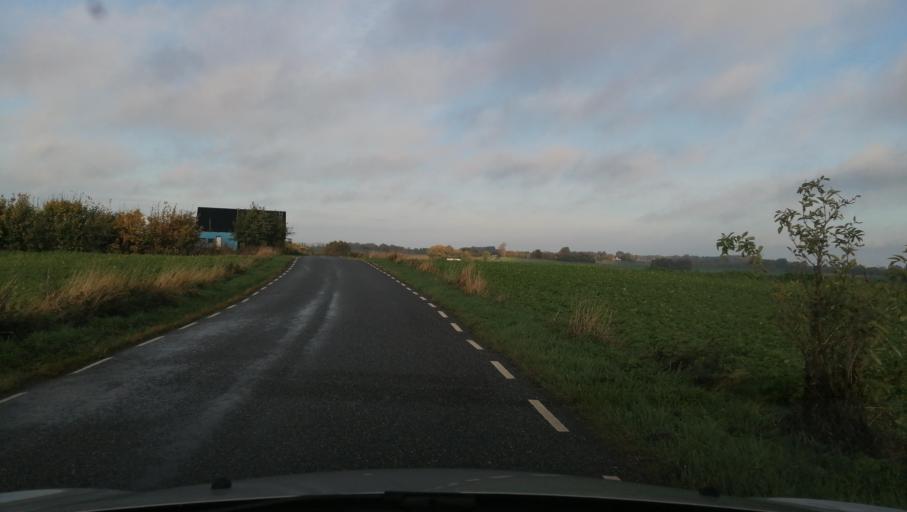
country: DK
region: Zealand
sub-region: Odsherred Kommune
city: Horve
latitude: 55.7449
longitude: 11.3892
